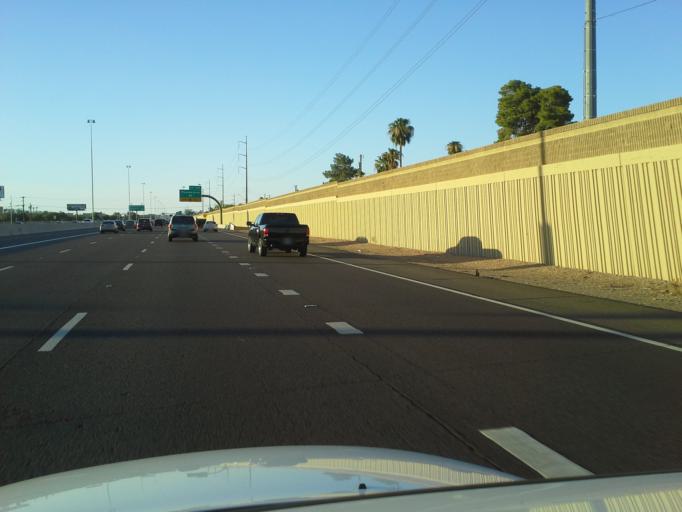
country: US
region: Arizona
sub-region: Maricopa County
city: Glendale
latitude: 33.6007
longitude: -112.1166
